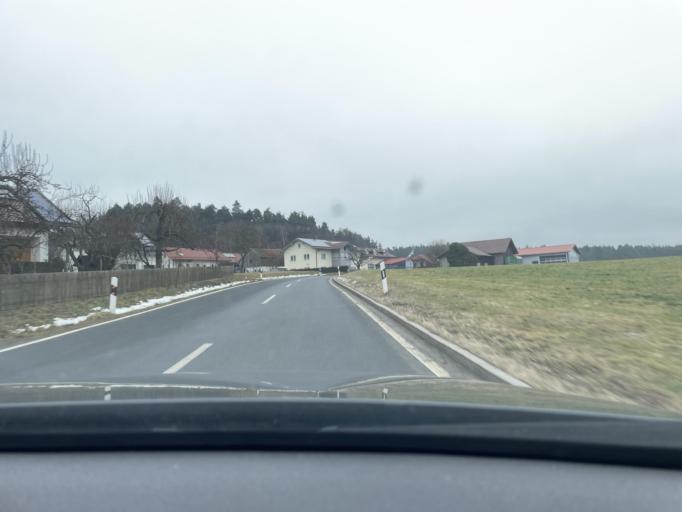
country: DE
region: Bavaria
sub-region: Upper Palatinate
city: Chamerau
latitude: 49.1868
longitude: 12.7151
